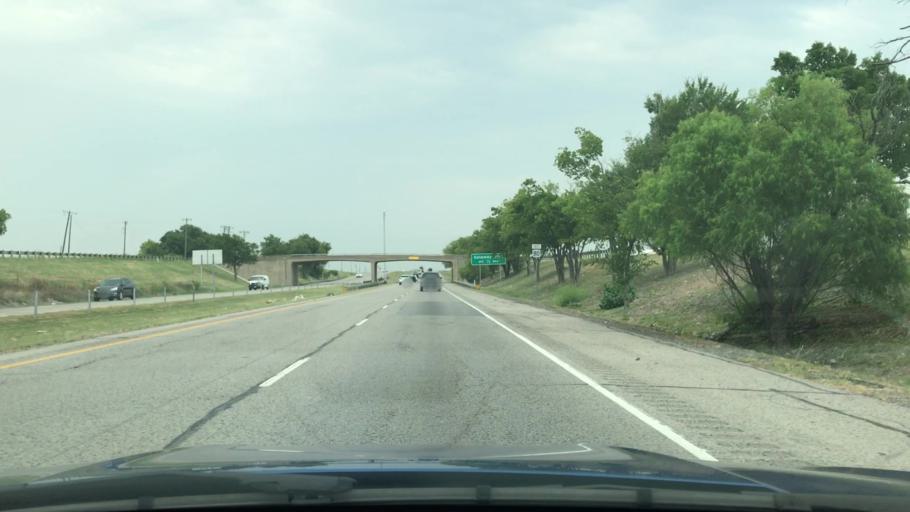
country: US
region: Texas
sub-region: Kaufman County
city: Forney
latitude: 32.7410
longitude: -96.4319
